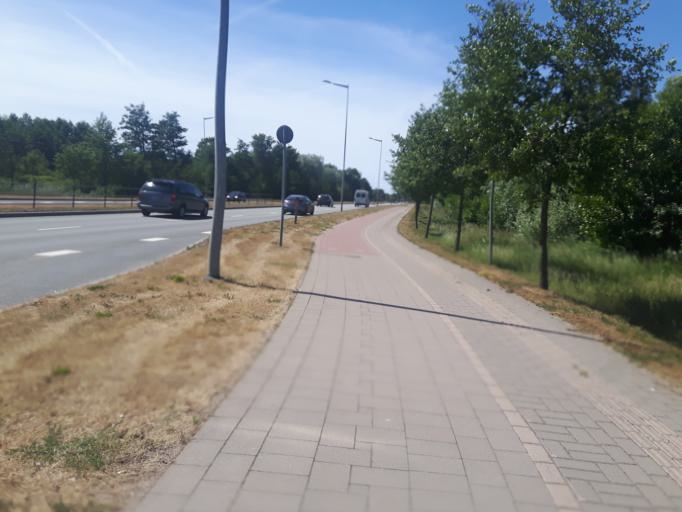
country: LV
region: Liepaja
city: Vec-Liepaja
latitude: 56.5362
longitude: 21.0782
